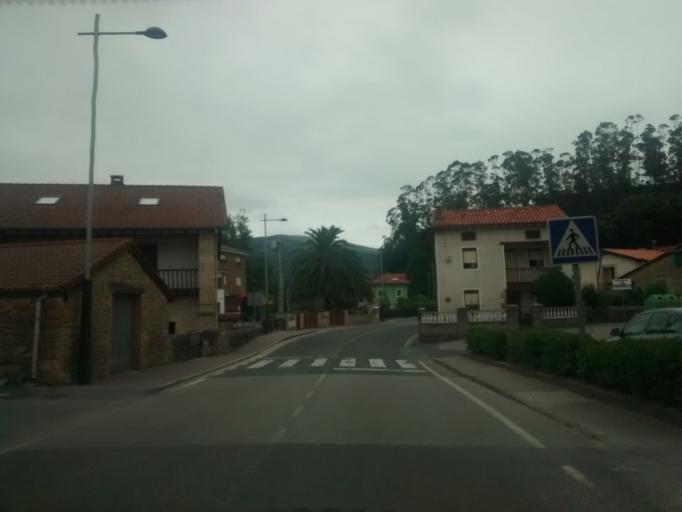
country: ES
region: Cantabria
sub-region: Provincia de Cantabria
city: Luzmela
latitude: 43.3192
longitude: -4.1912
